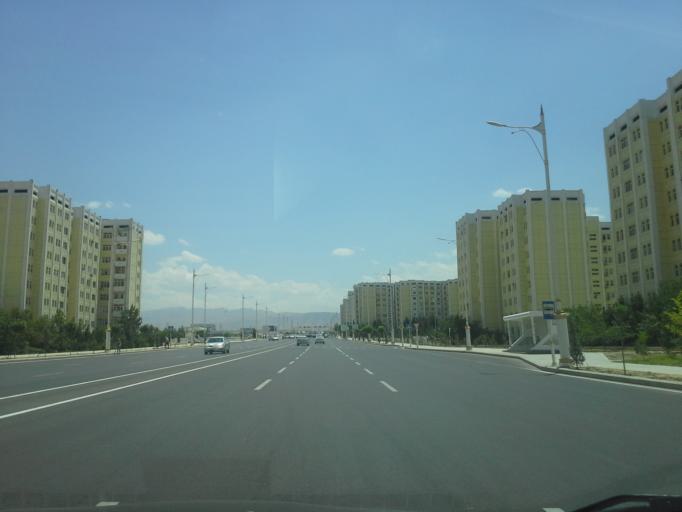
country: TM
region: Ahal
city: Ashgabat
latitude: 37.9093
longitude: 58.3977
